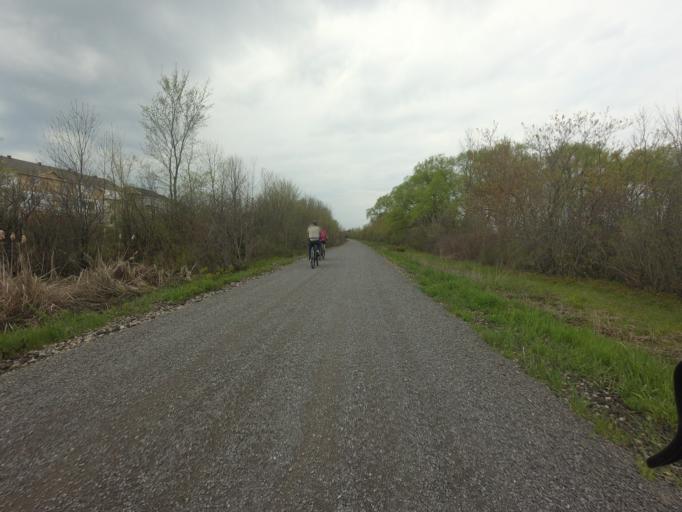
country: CA
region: Ontario
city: Carleton Place
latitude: 45.2200
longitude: -76.1868
